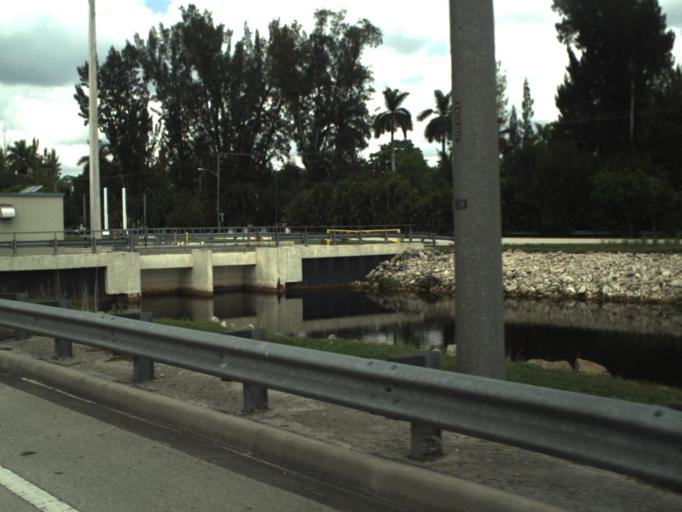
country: US
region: Florida
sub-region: Broward County
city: Cooper City
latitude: 26.0643
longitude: -80.2810
